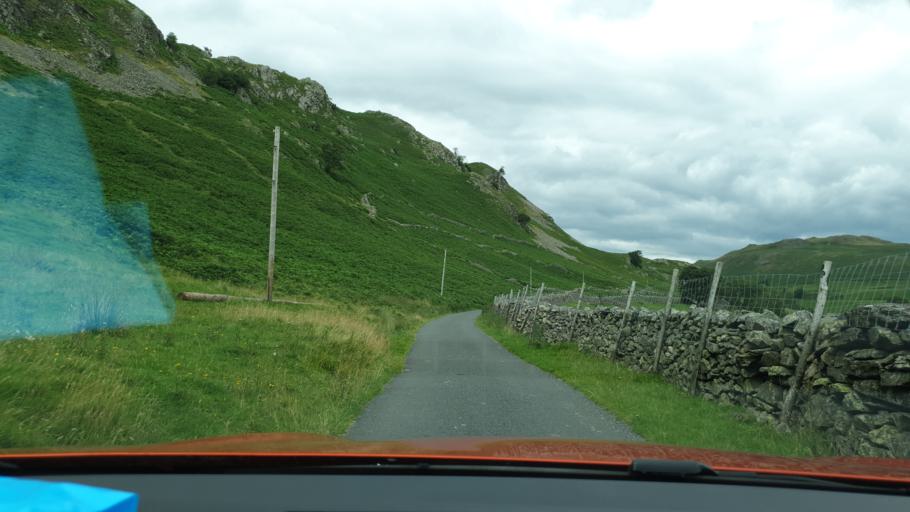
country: GB
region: England
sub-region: Cumbria
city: Ambleside
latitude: 54.5531
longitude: -2.8782
